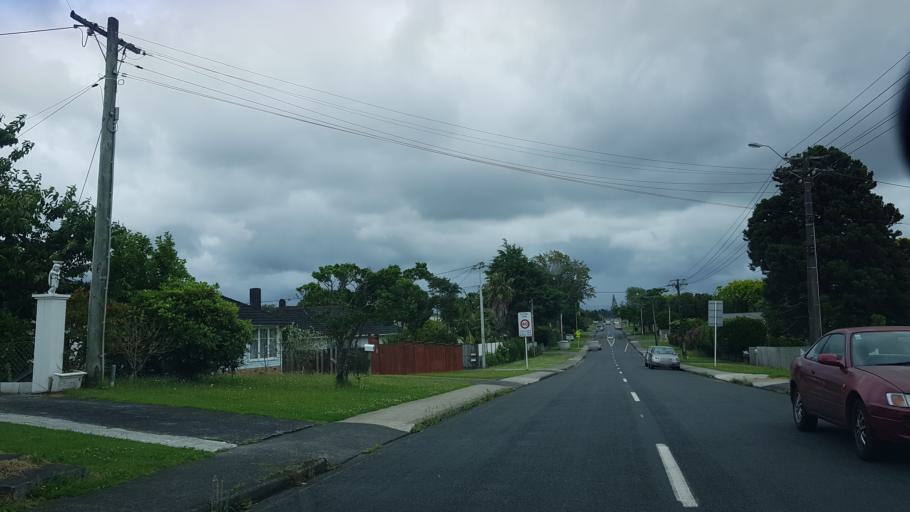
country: NZ
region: Auckland
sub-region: Auckland
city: Rosebank
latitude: -36.8338
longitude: 174.6538
